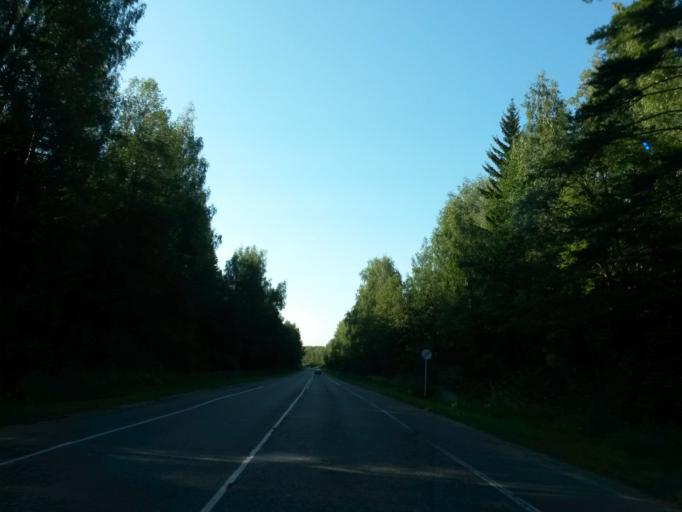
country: RU
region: Ivanovo
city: Pistsovo
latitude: 57.1101
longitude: 40.6500
